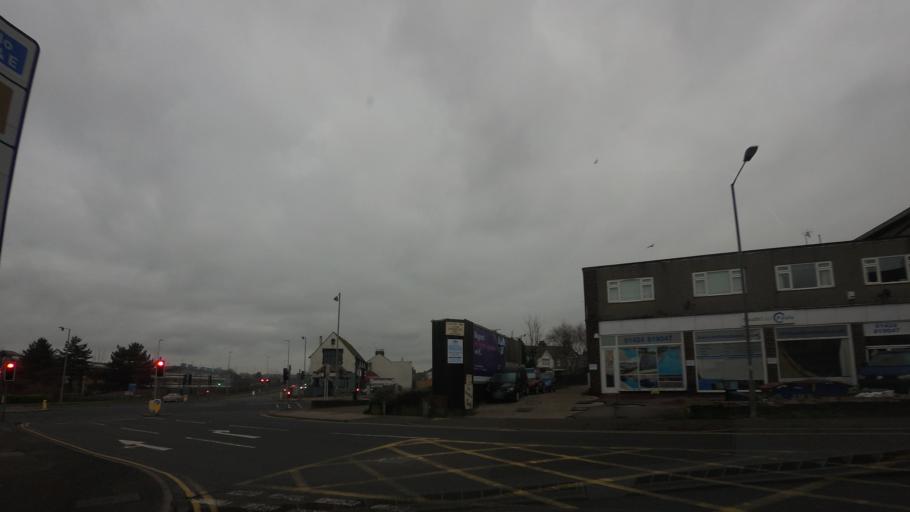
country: GB
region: England
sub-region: East Sussex
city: Bexhill-on-Sea
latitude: 50.8452
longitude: 0.4684
